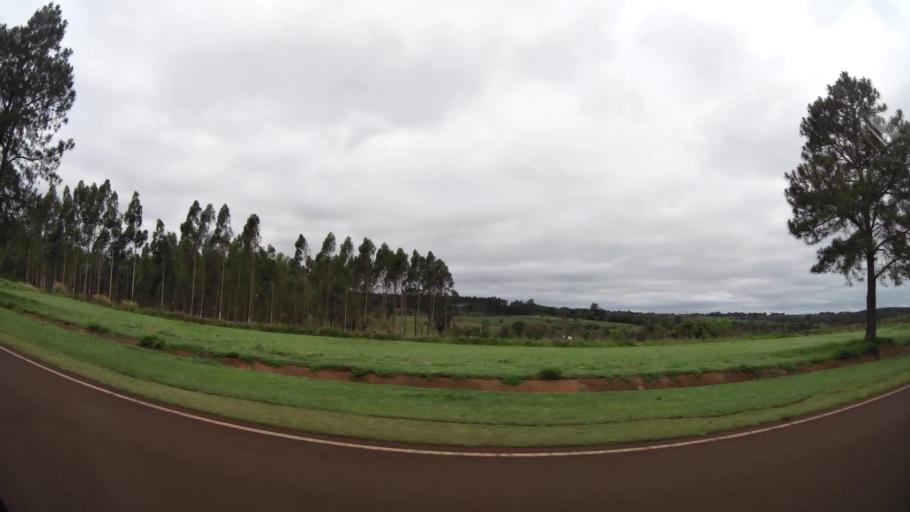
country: PY
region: Alto Parana
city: Colonia Yguazu
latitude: -25.4645
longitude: -54.8452
